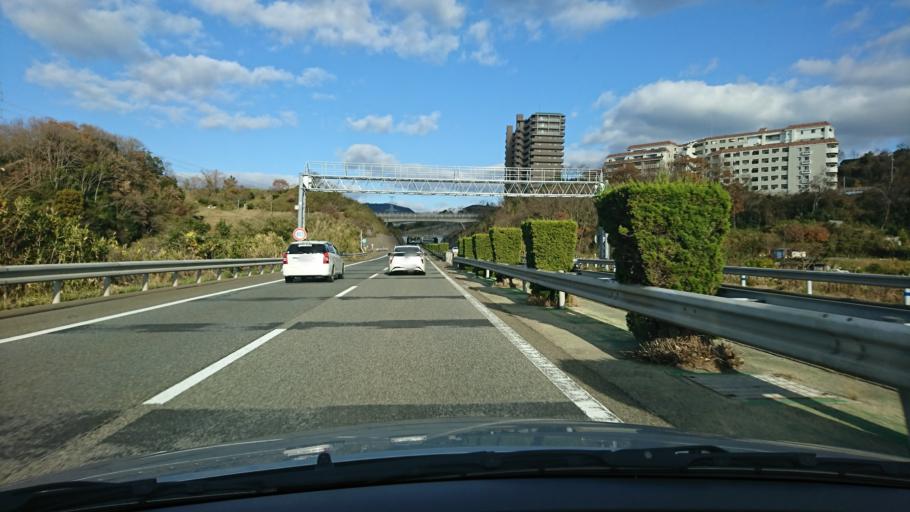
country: JP
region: Hyogo
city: Kobe
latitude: 34.7511
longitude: 135.1387
